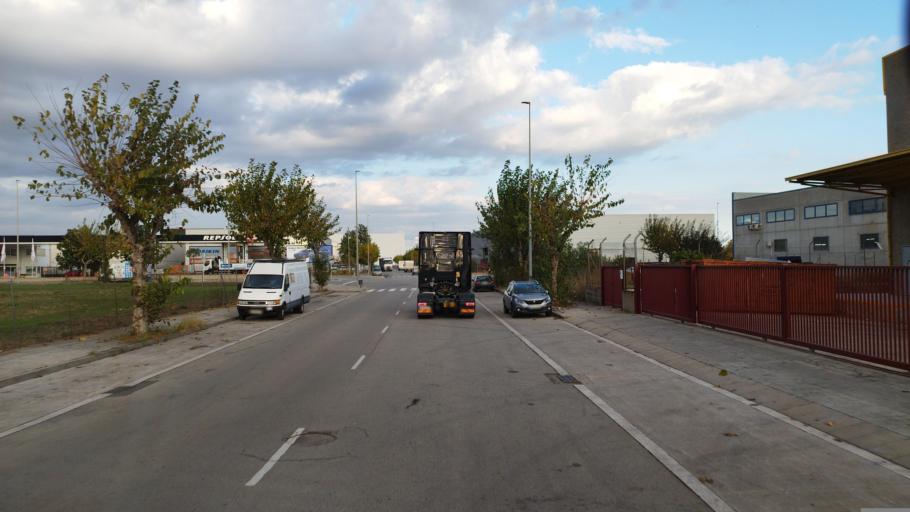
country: ES
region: Catalonia
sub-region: Provincia de Barcelona
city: Gava
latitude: 41.2970
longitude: 2.0145
